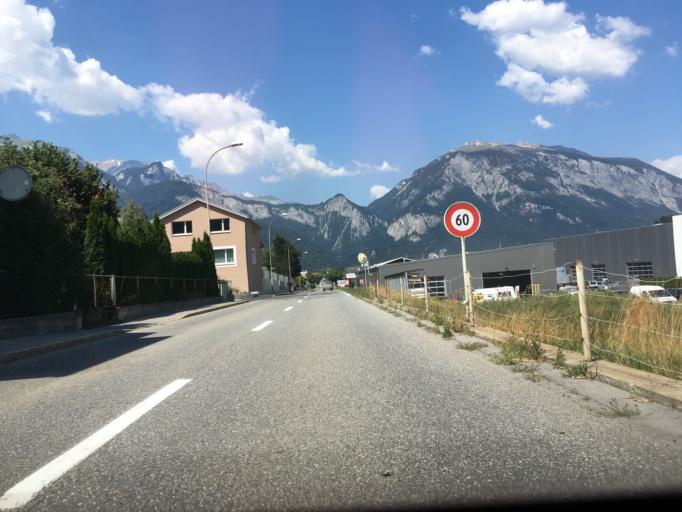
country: CH
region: Grisons
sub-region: Imboden District
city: Rhazuns
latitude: 46.8008
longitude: 9.3982
